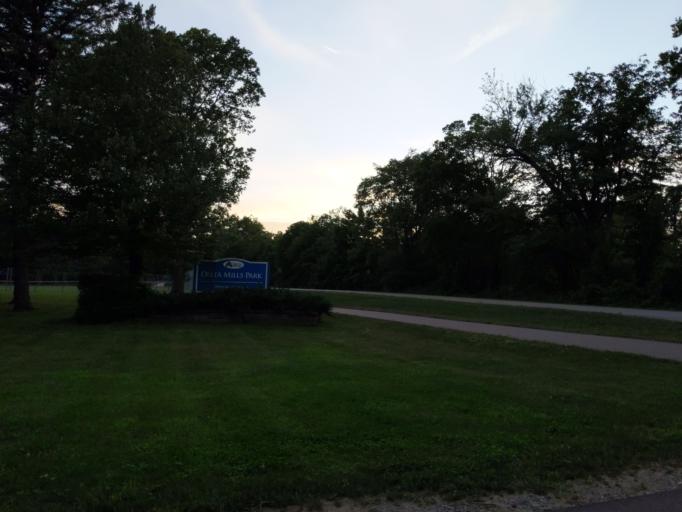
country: US
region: Michigan
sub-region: Eaton County
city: Waverly
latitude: 42.7598
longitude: -84.6514
